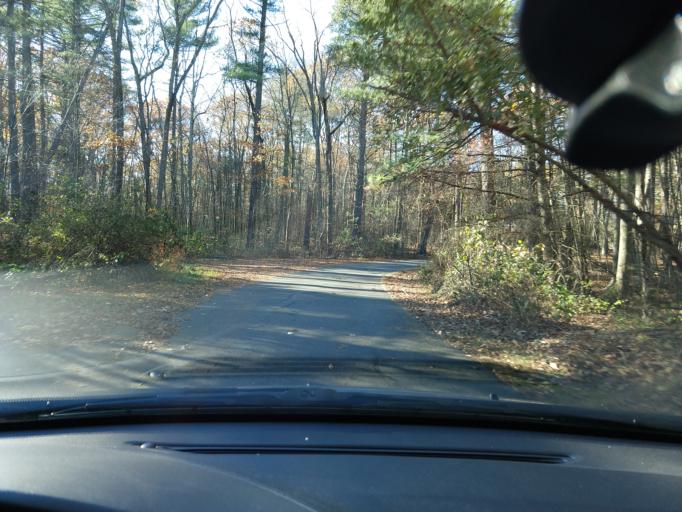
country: US
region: Massachusetts
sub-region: Middlesex County
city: Concord
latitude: 42.4943
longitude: -71.3379
